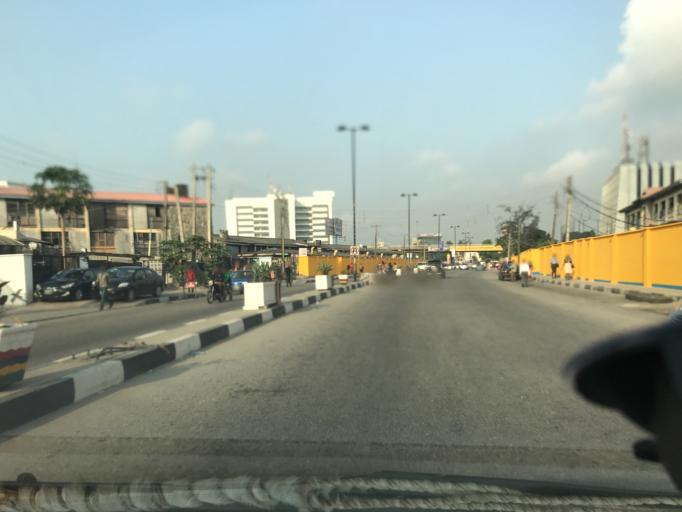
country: NG
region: Lagos
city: Ikoyi
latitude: 6.4438
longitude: 3.4296
